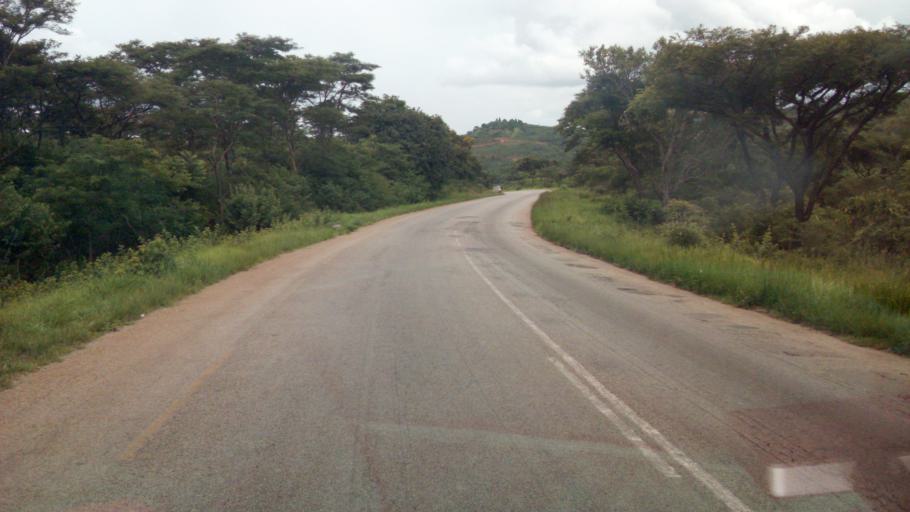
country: ZW
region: Mashonaland Central
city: Mazowe
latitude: -17.6351
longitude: 30.9758
